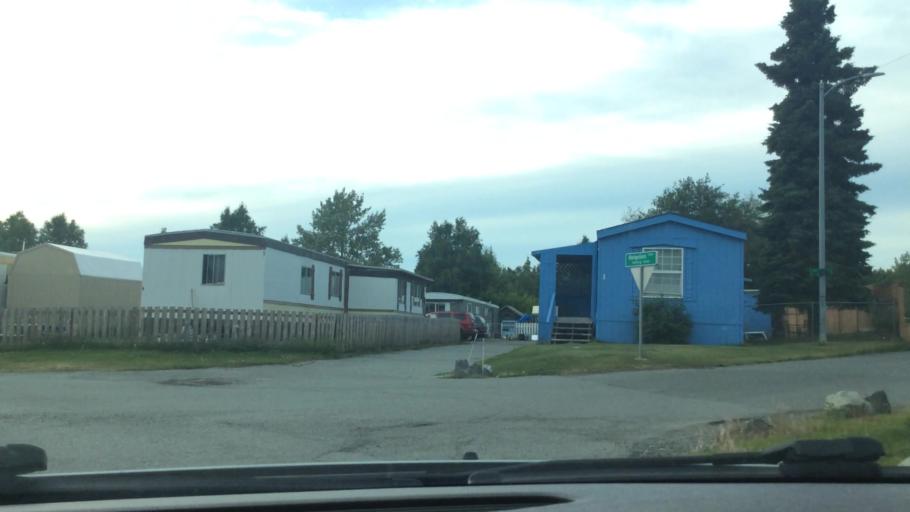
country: US
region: Alaska
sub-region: Anchorage Municipality
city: Anchorage
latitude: 61.1366
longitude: -149.8505
